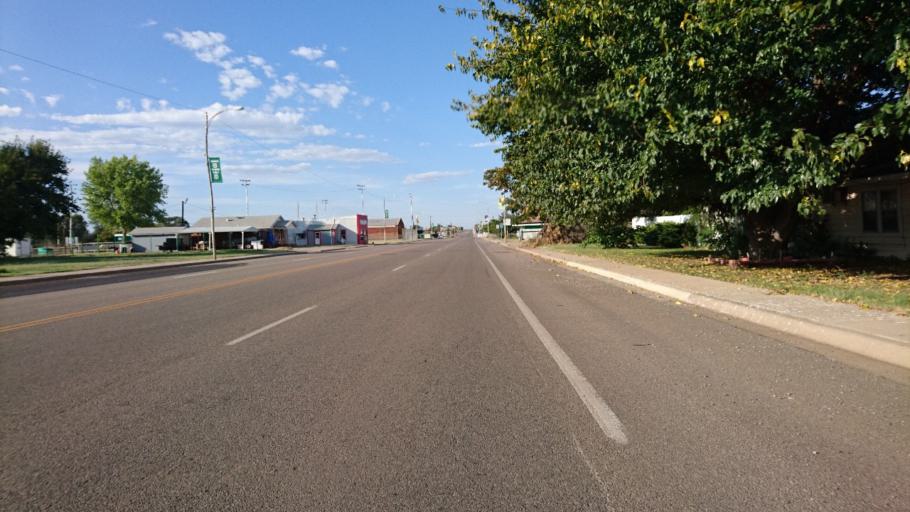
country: US
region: Texas
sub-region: Wheeler County
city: Shamrock
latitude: 35.2228
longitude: -100.2491
